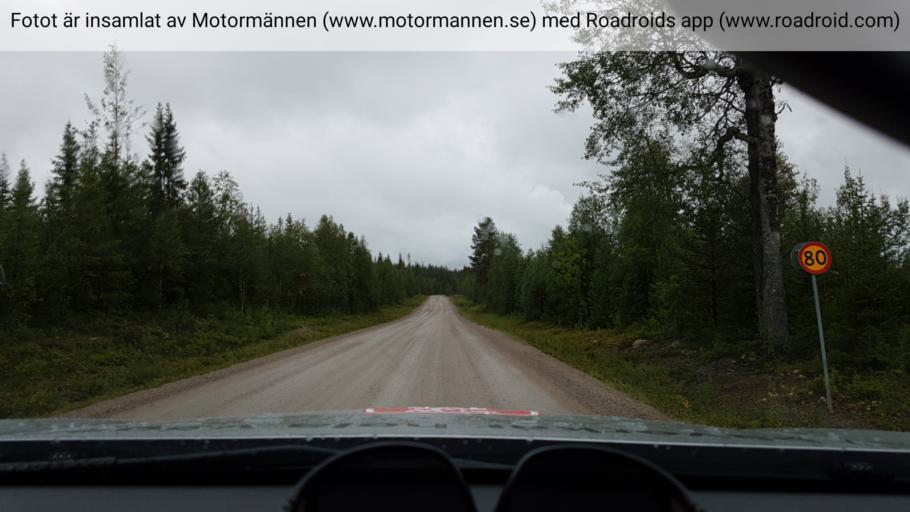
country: SE
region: Vaesterbotten
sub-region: Lycksele Kommun
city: Soderfors
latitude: 64.7584
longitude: 17.6578
